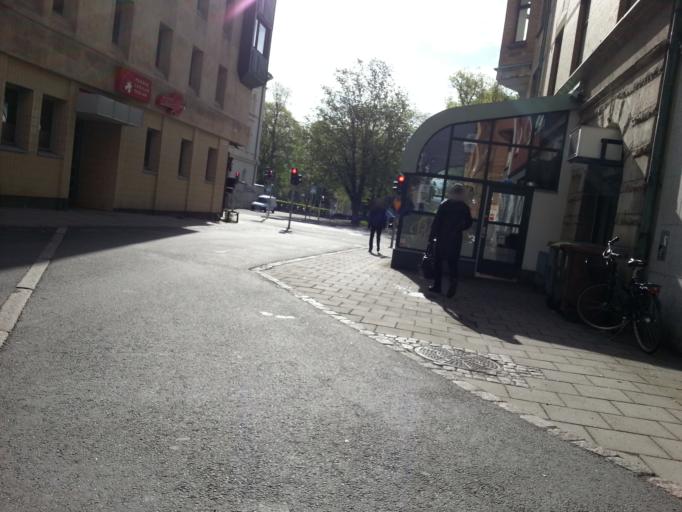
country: SE
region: Joenkoeping
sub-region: Jonkopings Kommun
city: Jonkoping
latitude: 57.7823
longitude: 14.1639
